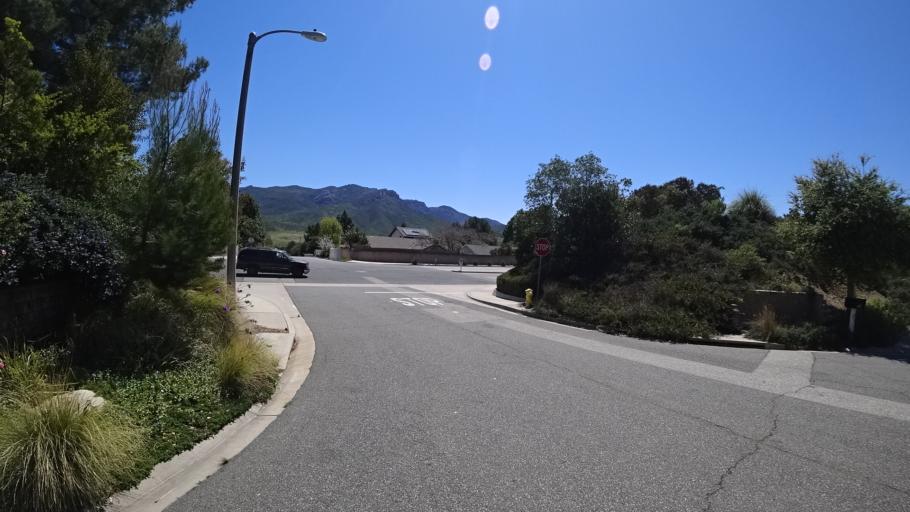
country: US
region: California
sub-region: Ventura County
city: Casa Conejo
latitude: 34.1608
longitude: -118.9659
